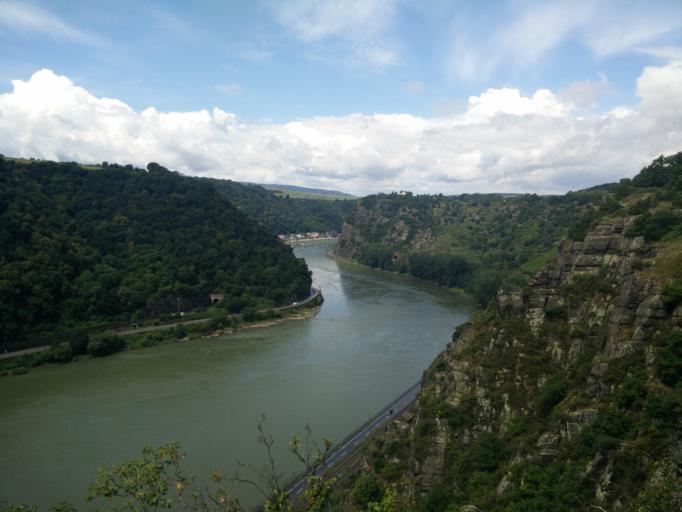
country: DE
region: Rheinland-Pfalz
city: Sankt Goarshausen
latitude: 50.1321
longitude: 7.7420
